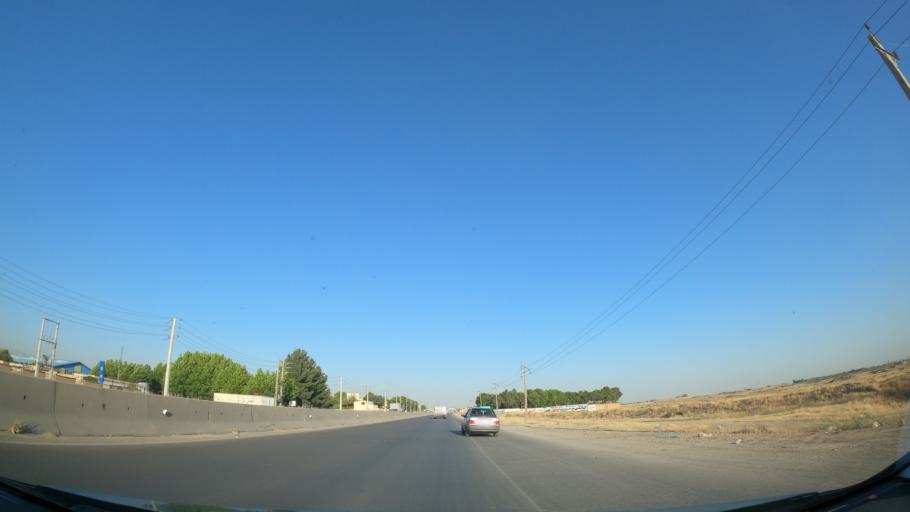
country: IR
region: Alborz
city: Hashtgerd
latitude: 35.9227
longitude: 50.7433
